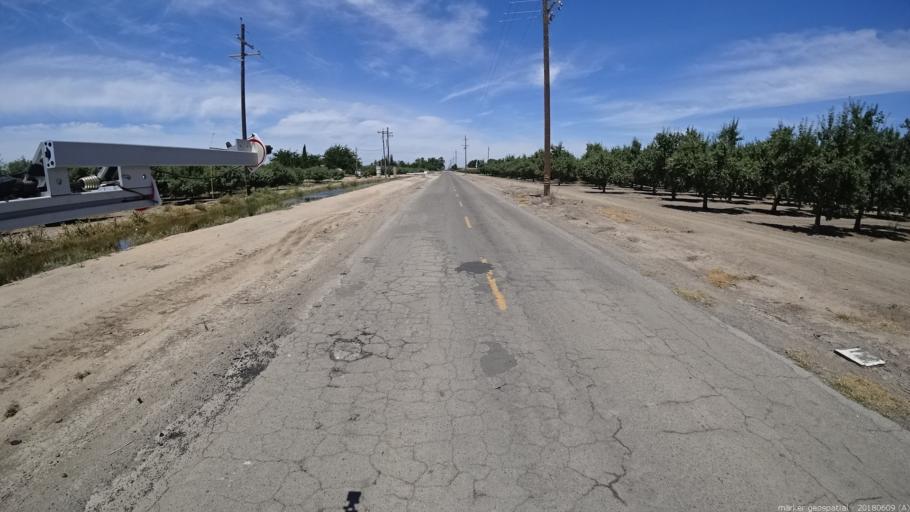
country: US
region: California
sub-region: Madera County
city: Parkwood
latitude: 36.8754
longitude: -120.1104
